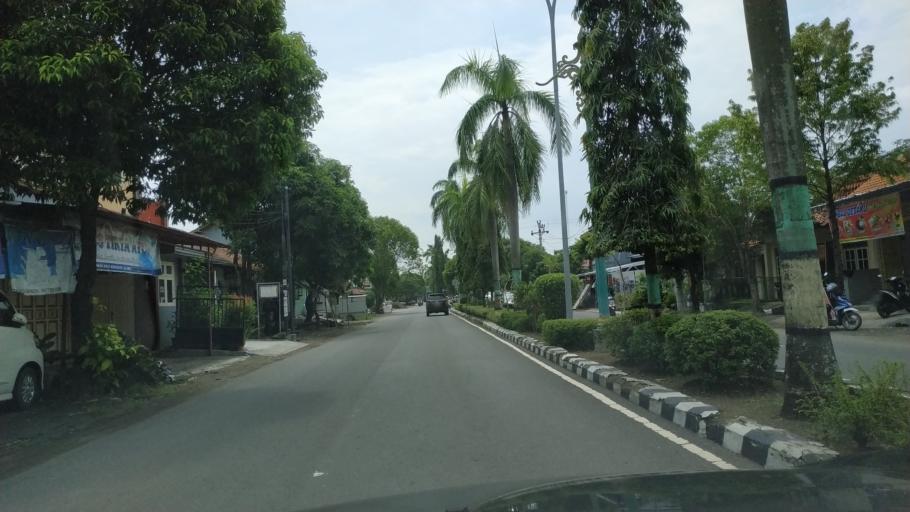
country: ID
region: Central Java
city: Slawi
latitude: -6.9838
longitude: 109.1270
